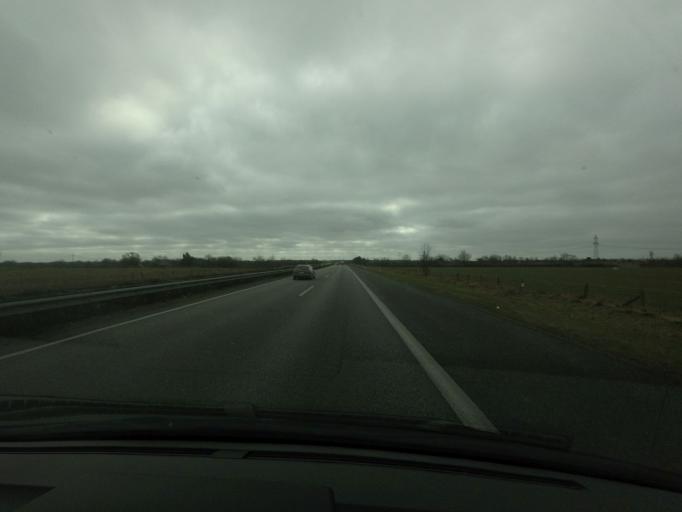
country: DE
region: Schleswig-Holstein
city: Oeversee
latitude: 54.6946
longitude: 9.4073
